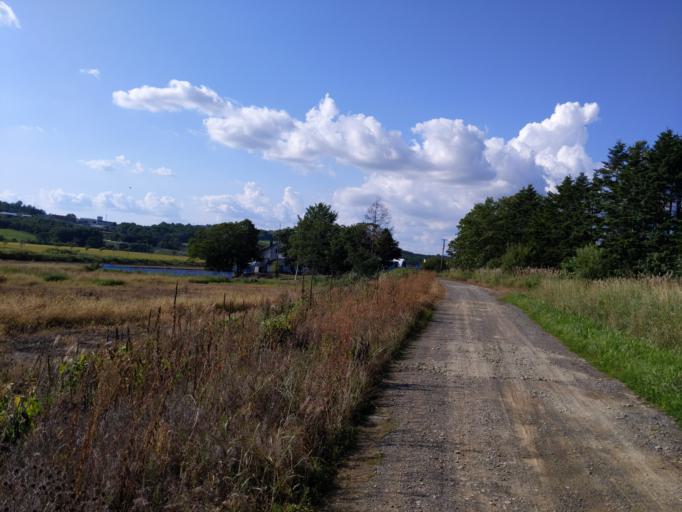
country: JP
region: Hokkaido
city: Iwamizawa
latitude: 43.1945
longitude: 141.8299
